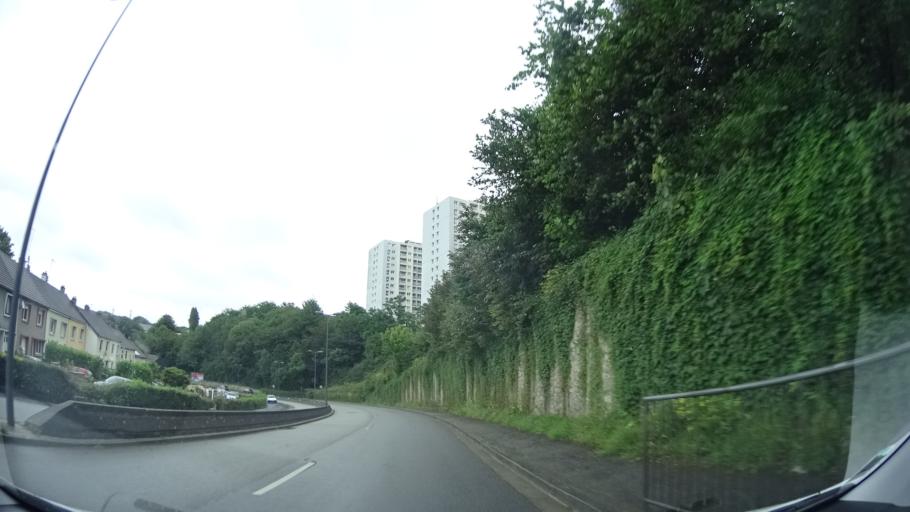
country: FR
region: Lower Normandy
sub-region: Departement de la Manche
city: Octeville
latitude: 49.6293
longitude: -1.6282
